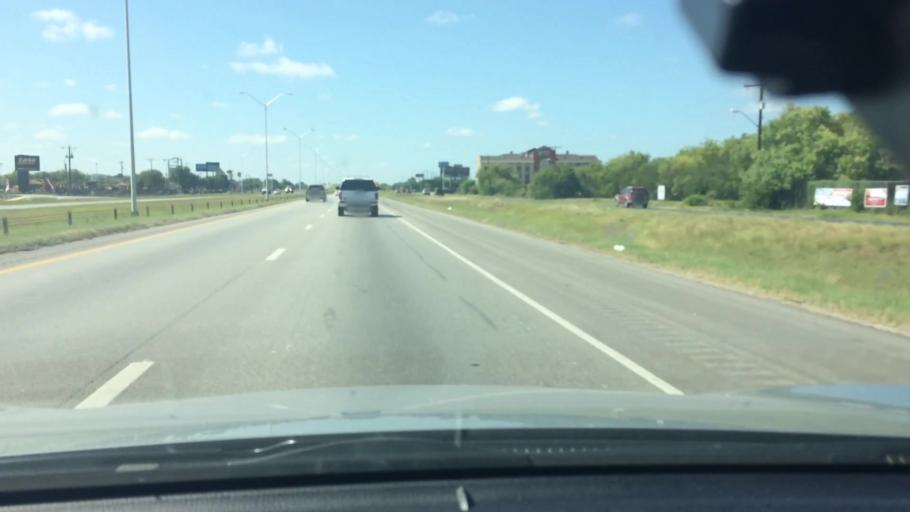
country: US
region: Texas
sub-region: Bexar County
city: China Grove
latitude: 29.4054
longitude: -98.3896
